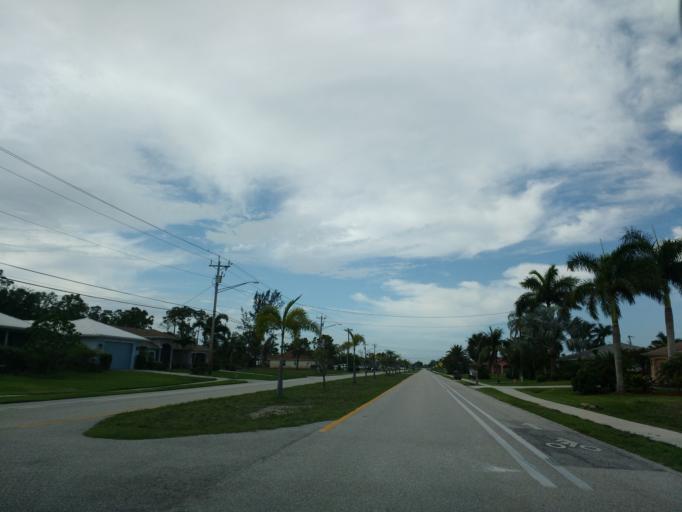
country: US
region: Florida
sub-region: Lee County
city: Cape Coral
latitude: 26.5832
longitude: -82.0241
